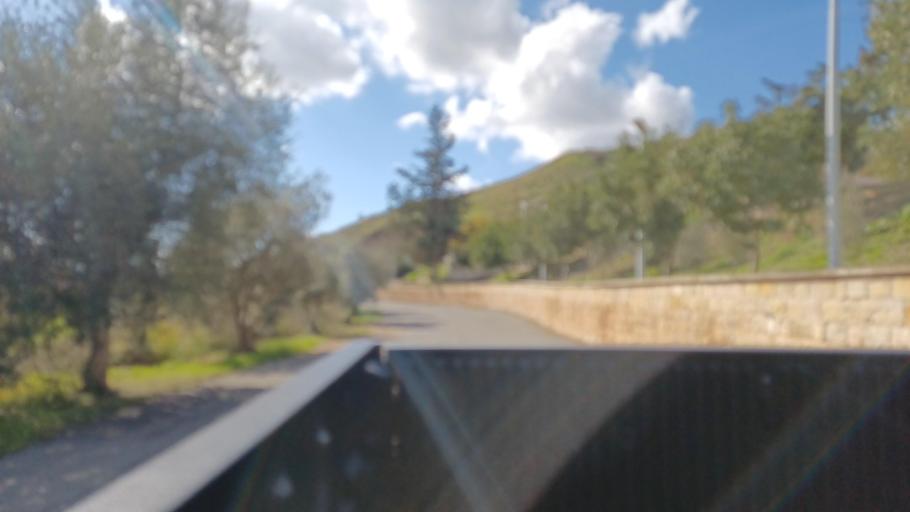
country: CY
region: Limassol
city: Pissouri
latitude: 34.7688
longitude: 32.6361
